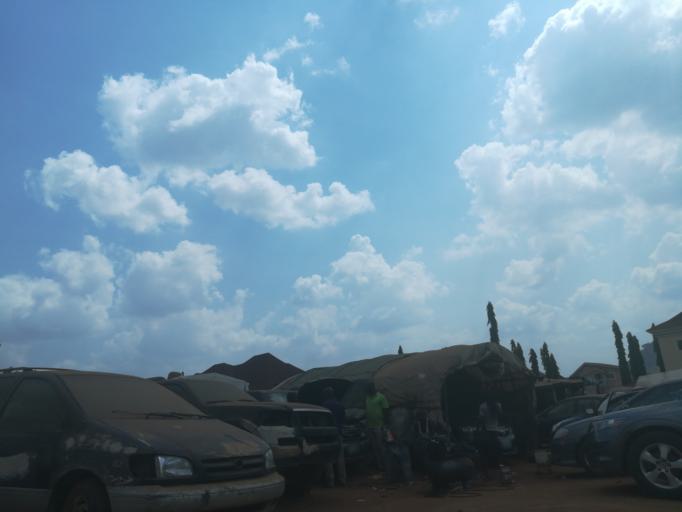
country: NG
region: Abuja Federal Capital Territory
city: Abuja
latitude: 9.0593
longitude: 7.4491
